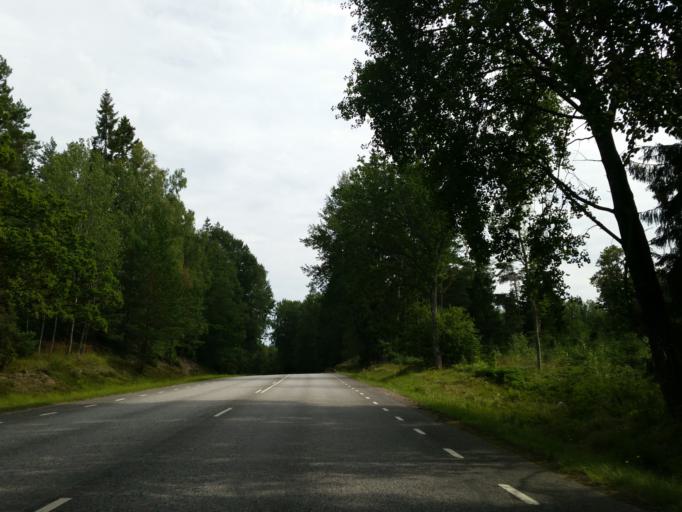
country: SE
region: Soedermanland
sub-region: Strangnas Kommun
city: Mariefred
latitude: 59.2389
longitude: 17.1941
